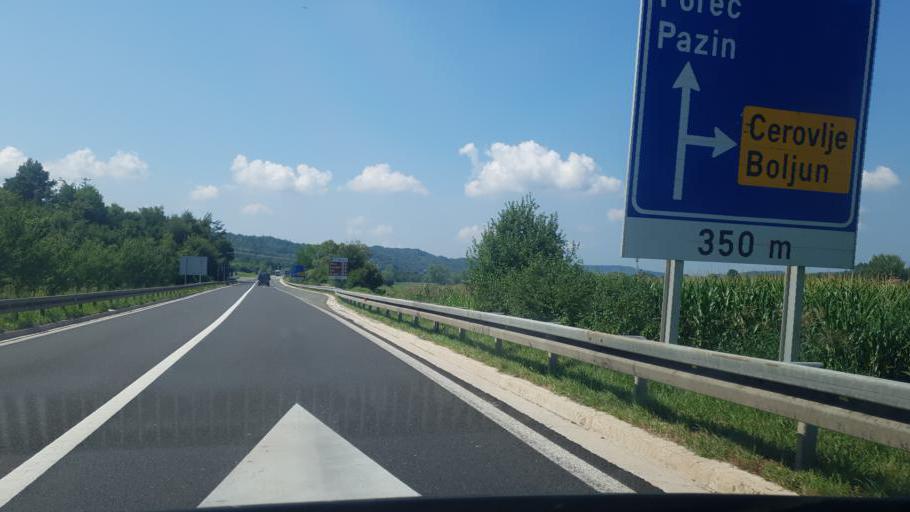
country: HR
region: Istarska
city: Pazin
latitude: 45.2788
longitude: 14.0200
